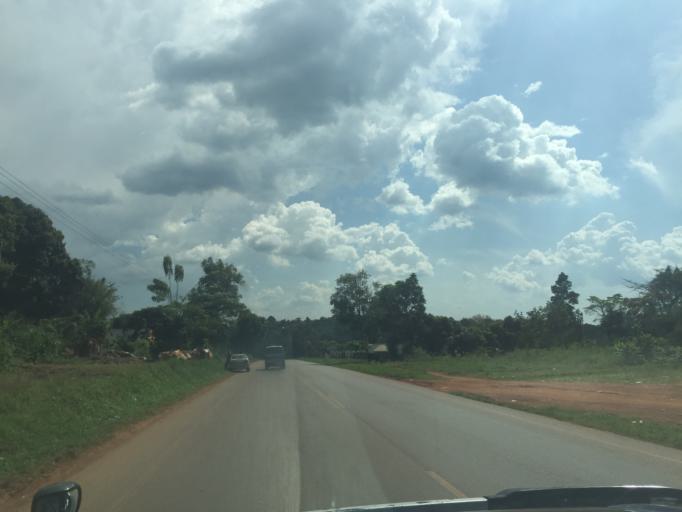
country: UG
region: Central Region
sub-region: Luwero District
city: Wobulenzi
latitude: 0.7026
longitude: 32.5244
